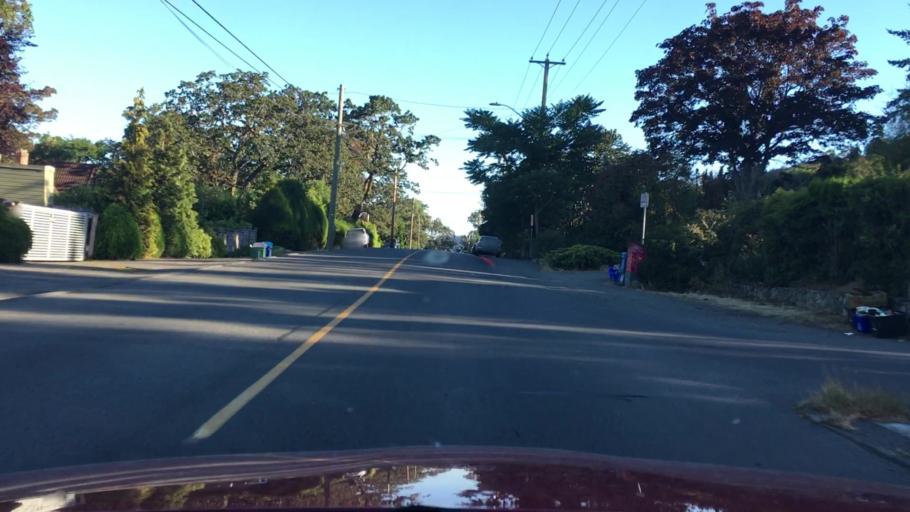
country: CA
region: British Columbia
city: Oak Bay
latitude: 48.4535
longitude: -123.3269
